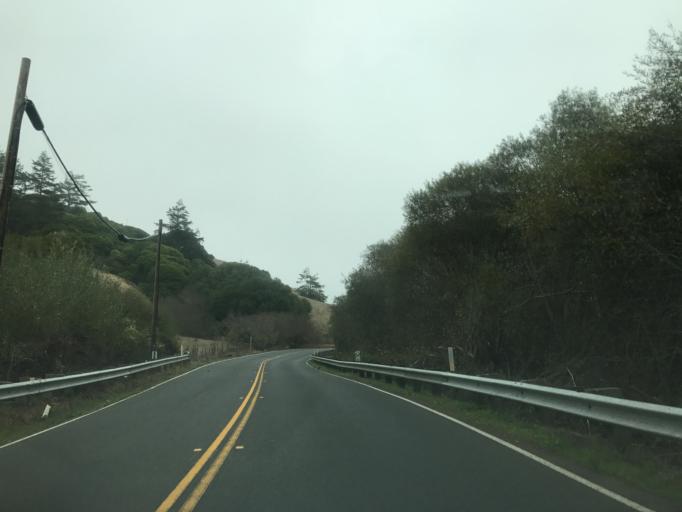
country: US
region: California
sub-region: Sonoma County
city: Monte Rio
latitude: 38.4474
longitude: -123.0862
